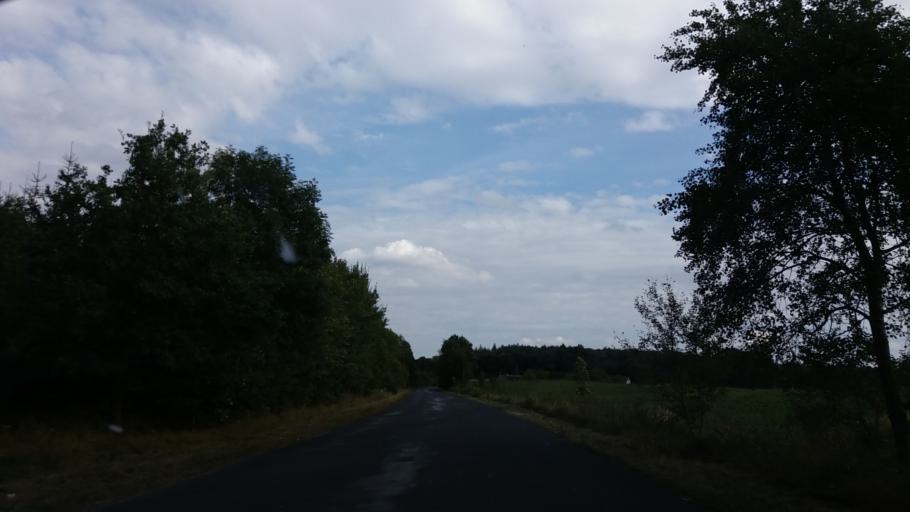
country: PL
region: West Pomeranian Voivodeship
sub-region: Powiat stargardzki
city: Dolice
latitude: 53.2423
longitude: 15.2316
